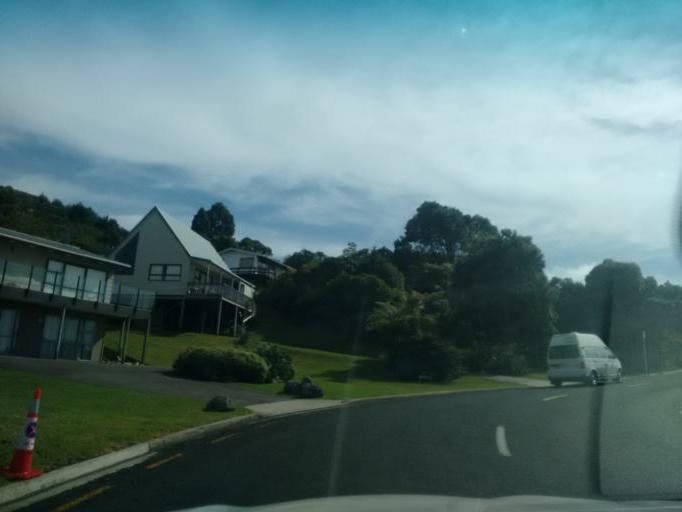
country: NZ
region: Waikato
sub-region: Thames-Coromandel District
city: Whitianga
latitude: -36.8365
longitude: 175.7990
